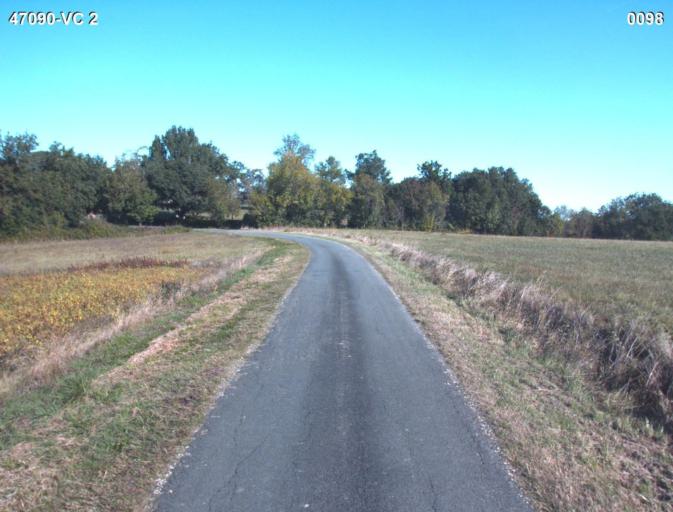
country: FR
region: Aquitaine
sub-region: Departement du Lot-et-Garonne
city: Vianne
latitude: 44.1902
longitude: 0.3670
